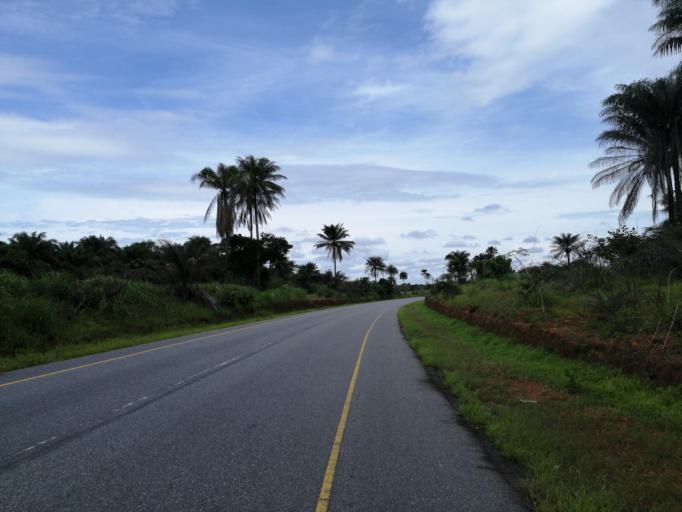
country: SL
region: Northern Province
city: Port Loko
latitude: 8.7475
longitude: -12.9207
